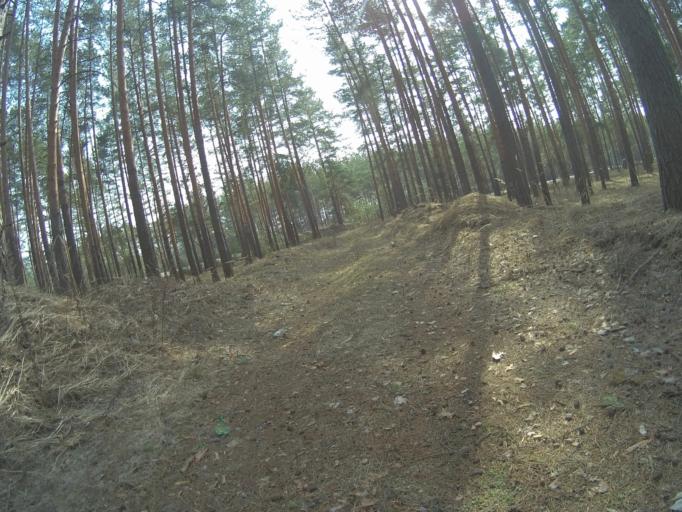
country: RU
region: Vladimir
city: Kommunar
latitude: 56.0384
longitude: 40.4265
